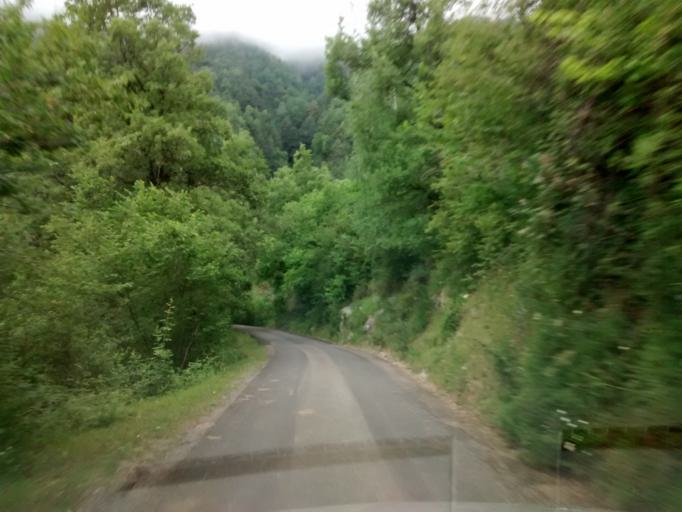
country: ES
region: Aragon
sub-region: Provincia de Huesca
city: Puertolas
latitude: 42.5919
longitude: 0.1266
